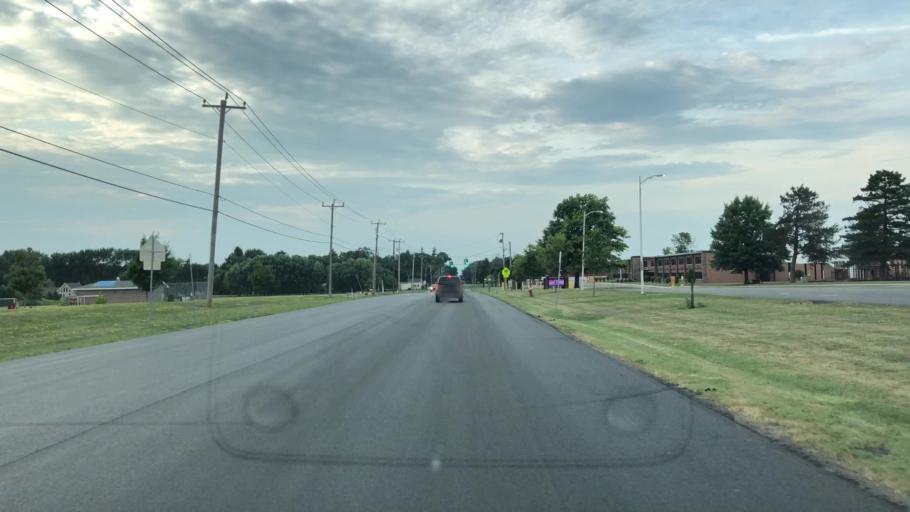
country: US
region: New York
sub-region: Erie County
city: Elma Center
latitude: 42.8338
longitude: -78.6060
